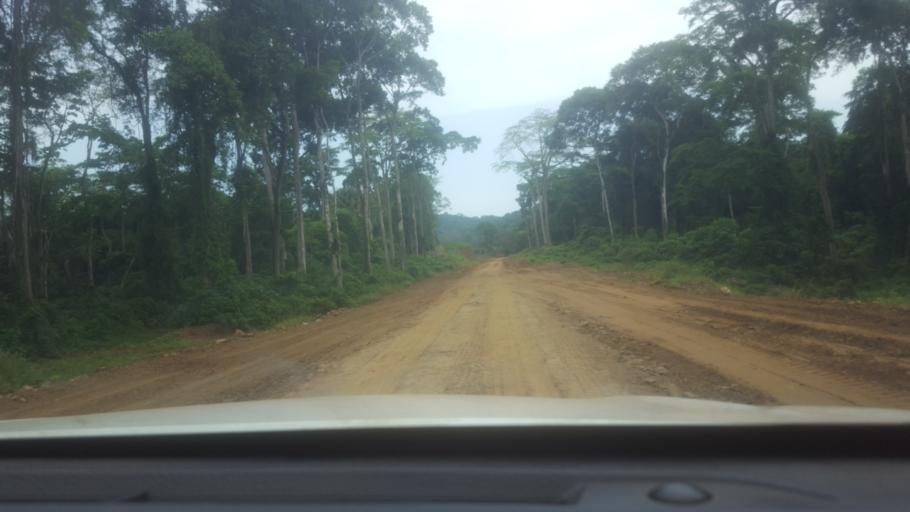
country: ET
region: Southern Nations, Nationalities, and People's Region
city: Tippi
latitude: 7.5216
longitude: 34.9941
